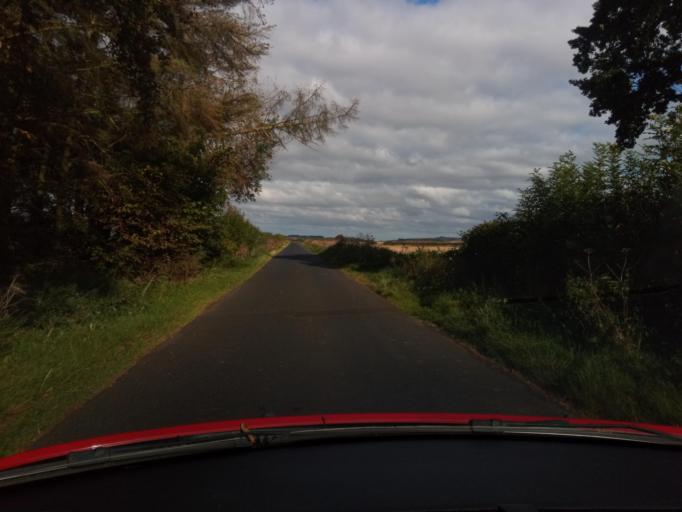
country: GB
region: Scotland
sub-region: The Scottish Borders
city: Kelso
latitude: 55.5640
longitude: -2.4185
